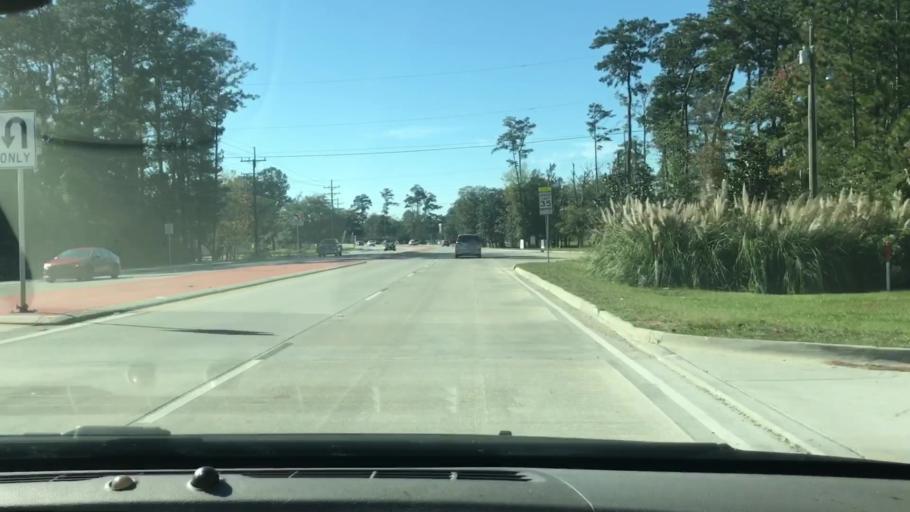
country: US
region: Louisiana
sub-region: Saint Tammany Parish
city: Covington
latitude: 30.4591
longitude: -90.1262
